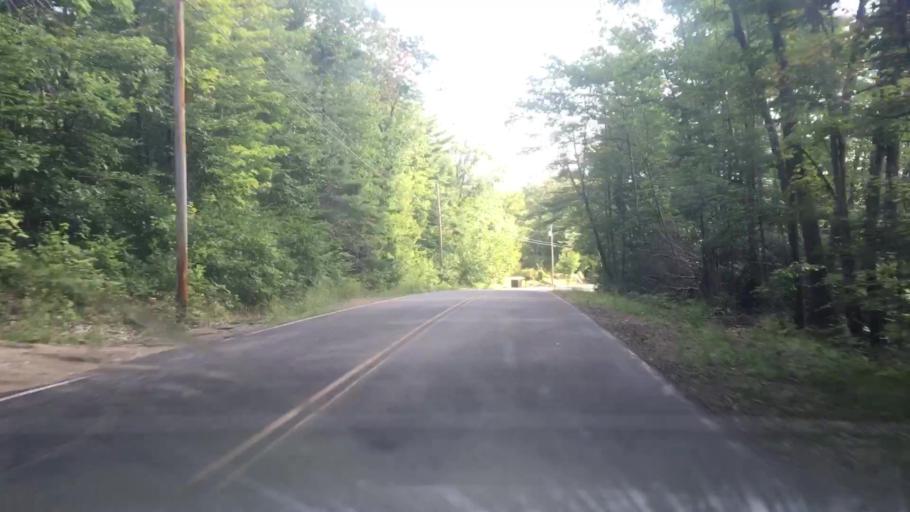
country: US
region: Maine
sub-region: Kennebec County
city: Pittston
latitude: 44.1665
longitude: -69.7893
